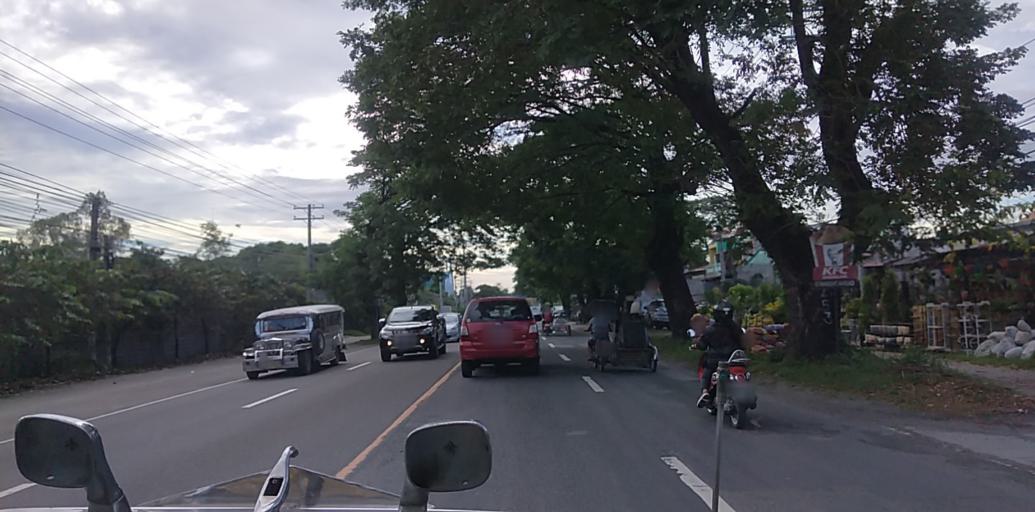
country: PH
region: Central Luzon
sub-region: Province of Pampanga
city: Telabastagan
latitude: 15.0957
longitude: 120.6249
